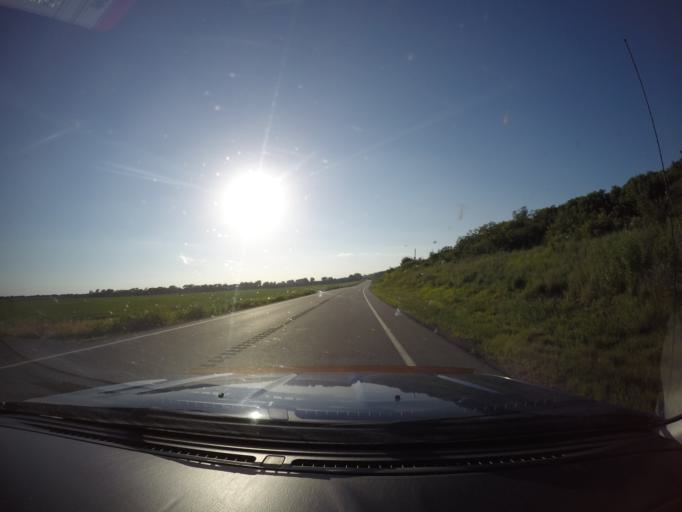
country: US
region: Kansas
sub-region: Pottawatomie County
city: Saint Marys
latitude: 39.1756
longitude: -96.0275
